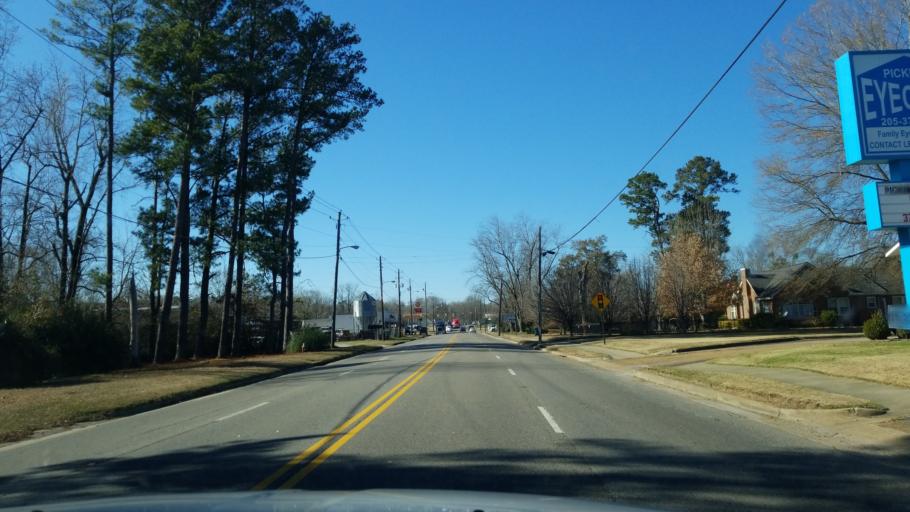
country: US
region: Alabama
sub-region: Pickens County
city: Reform
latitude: 33.3779
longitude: -88.0124
